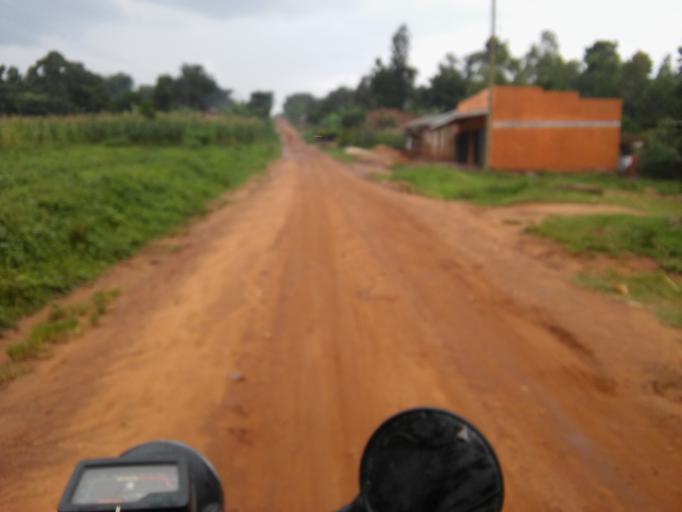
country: UG
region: Eastern Region
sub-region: Mbale District
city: Mbale
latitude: 1.0175
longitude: 34.1846
